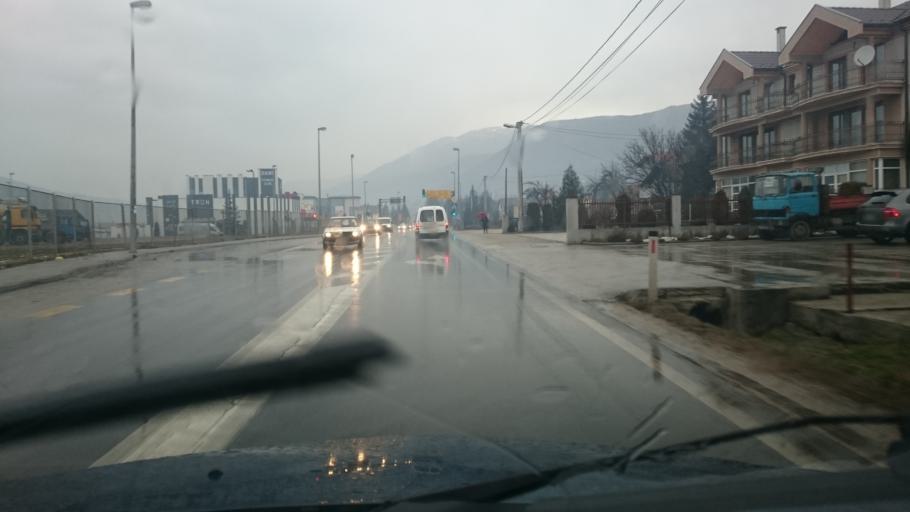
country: BA
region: Federation of Bosnia and Herzegovina
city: Travnik
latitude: 44.2063
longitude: 17.7170
